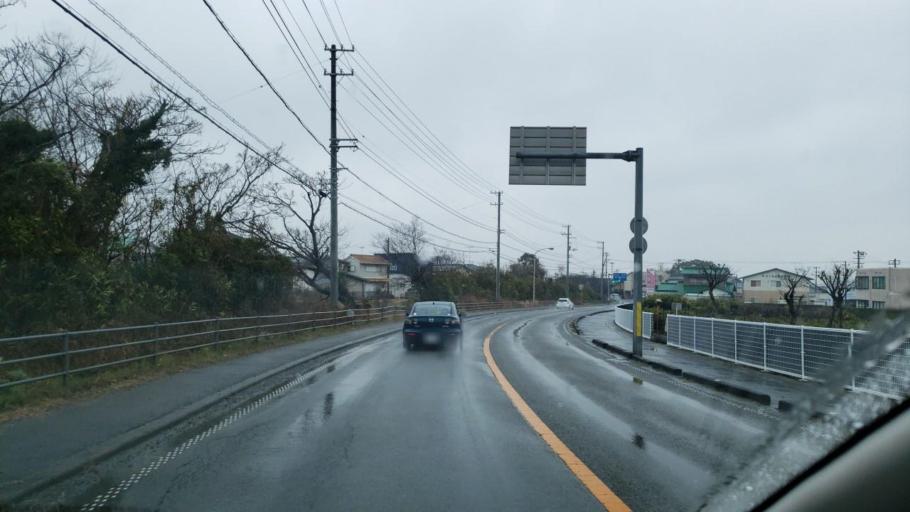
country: JP
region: Tokushima
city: Tokushima-shi
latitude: 34.1582
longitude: 134.5086
